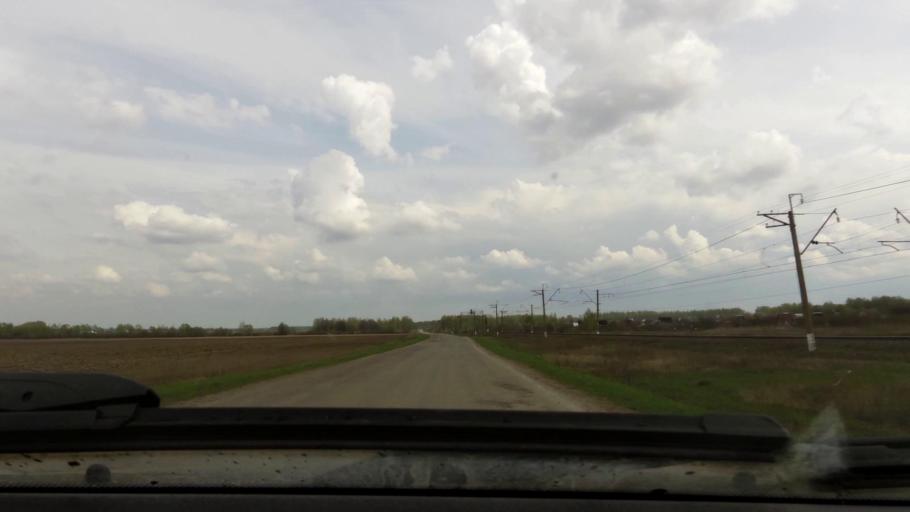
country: RU
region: Rjazan
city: Bagramovo
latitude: 54.7077
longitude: 39.3178
